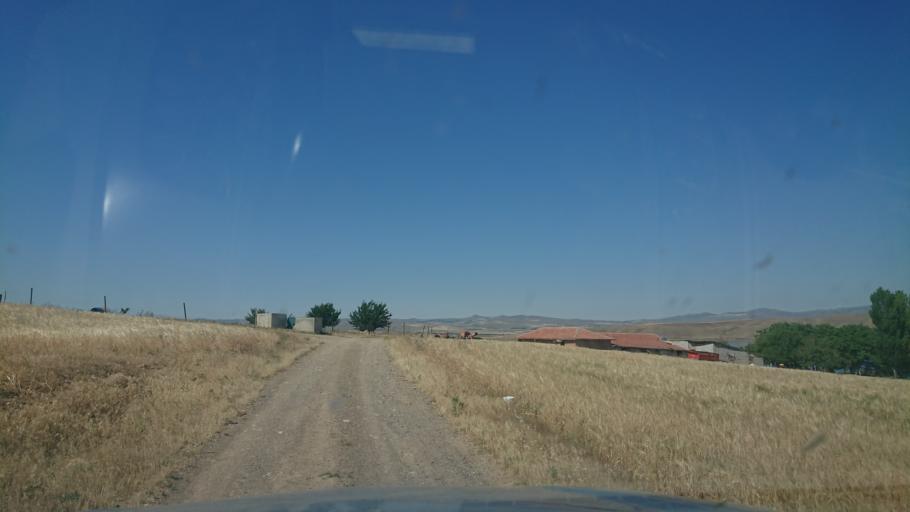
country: TR
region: Ankara
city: Evren
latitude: 39.0518
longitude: 33.8782
